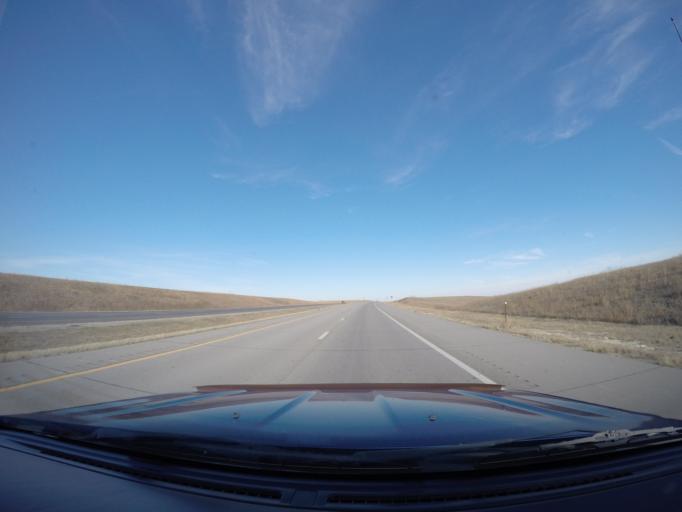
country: US
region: Kansas
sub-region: Cloud County
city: Concordia
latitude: 39.4868
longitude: -97.6664
